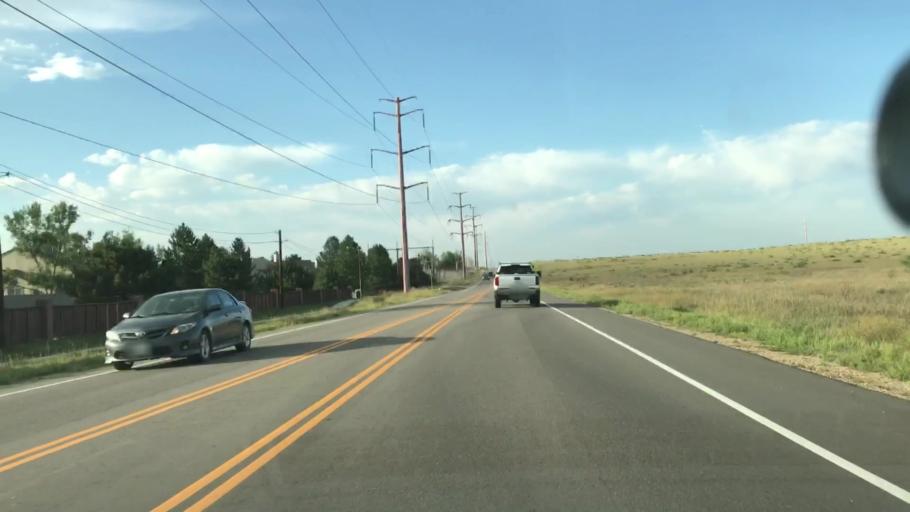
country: US
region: Colorado
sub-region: Boulder County
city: Gunbarrel
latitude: 40.0662
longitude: -105.1785
